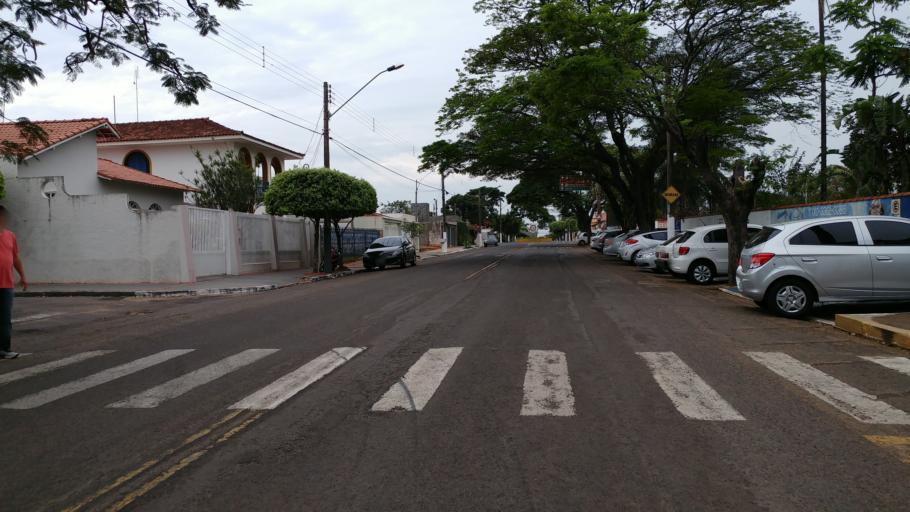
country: BR
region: Sao Paulo
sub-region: Paraguacu Paulista
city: Paraguacu Paulista
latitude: -22.4120
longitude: -50.5842
